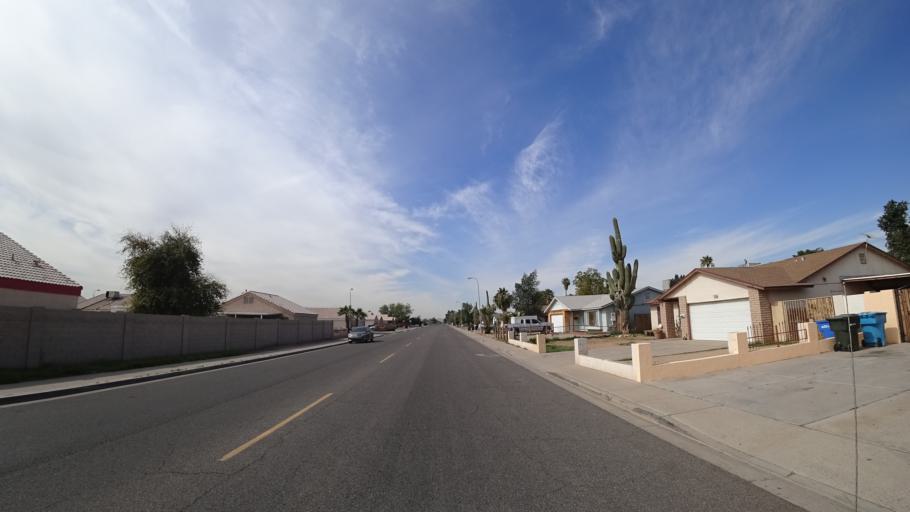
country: US
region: Arizona
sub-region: Maricopa County
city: Tolleson
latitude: 33.4871
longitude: -112.2387
